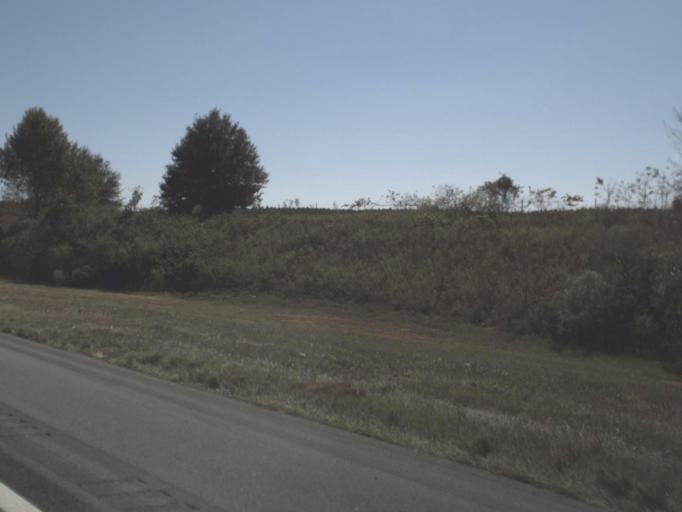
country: US
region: Florida
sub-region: Lake County
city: Howie In The Hills
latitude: 28.6584
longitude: -81.8201
